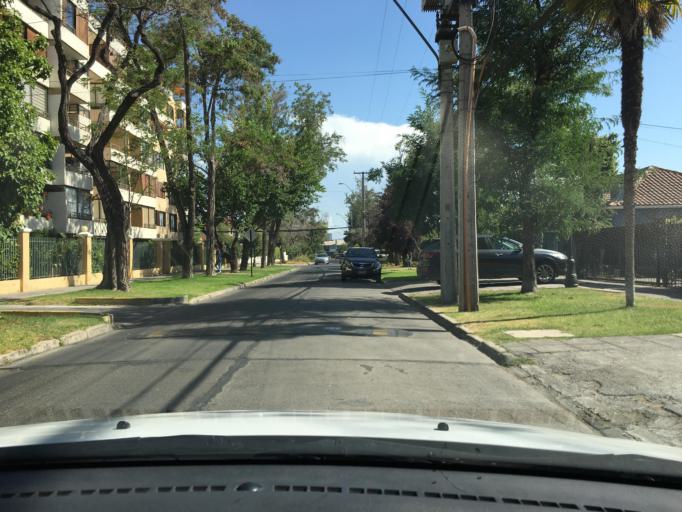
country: CL
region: Santiago Metropolitan
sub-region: Provincia de Santiago
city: Villa Presidente Frei, Nunoa, Santiago, Chile
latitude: -33.4422
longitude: -70.5909
